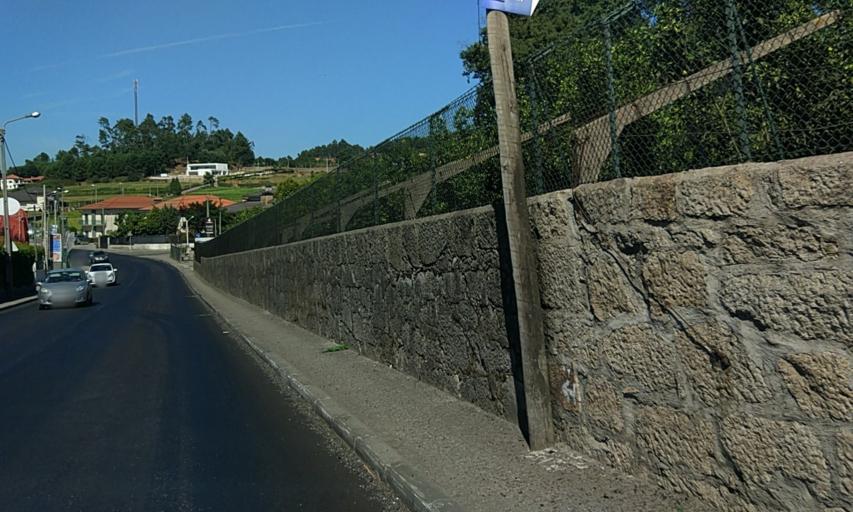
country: PT
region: Porto
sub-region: Trofa
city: Sao Romao do Coronado
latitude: 41.2971
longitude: -8.5974
